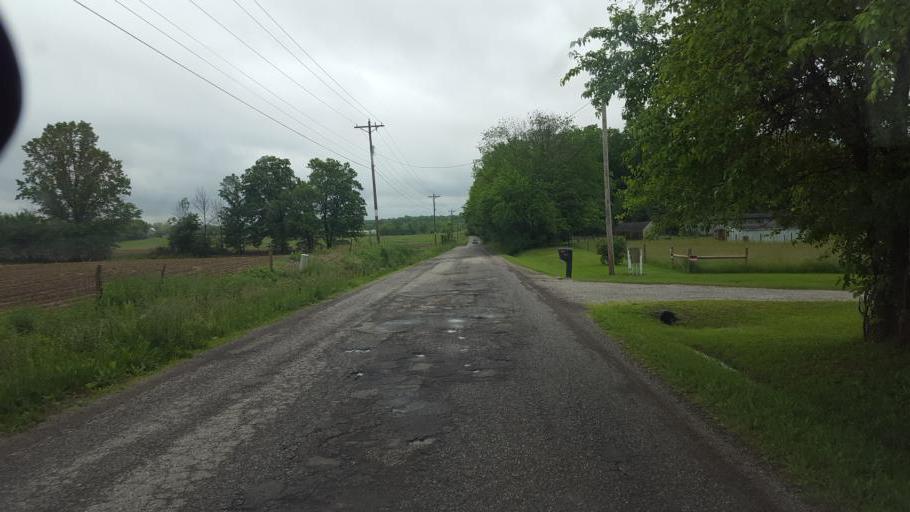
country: US
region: Ohio
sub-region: Morrow County
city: Mount Gilead
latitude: 40.4670
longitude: -82.7829
